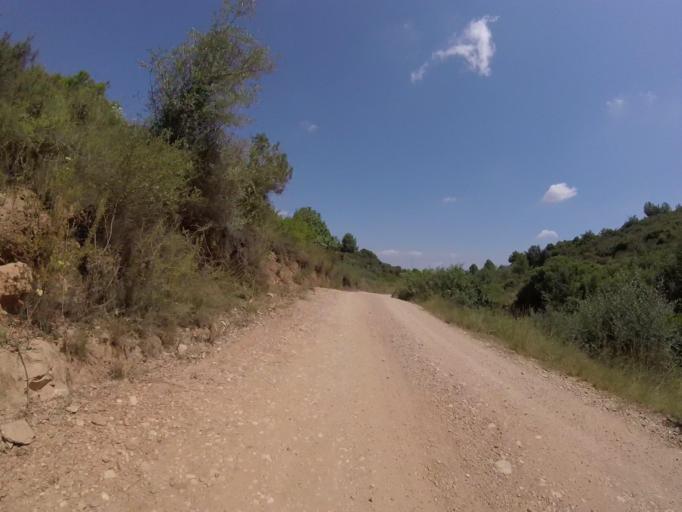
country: ES
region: Valencia
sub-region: Provincia de Castello
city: Torreblanca
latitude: 40.2282
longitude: 0.1574
